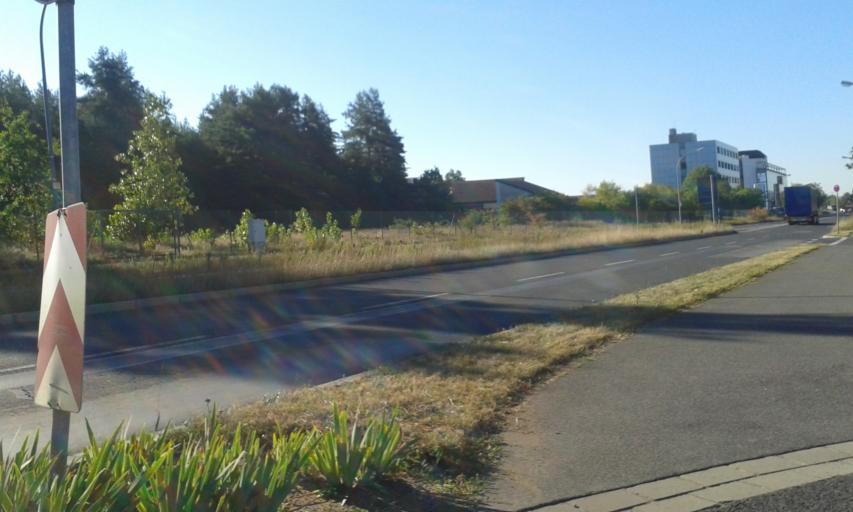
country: DE
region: Bavaria
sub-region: Upper Franconia
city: Bamberg
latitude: 49.8869
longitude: 10.9220
